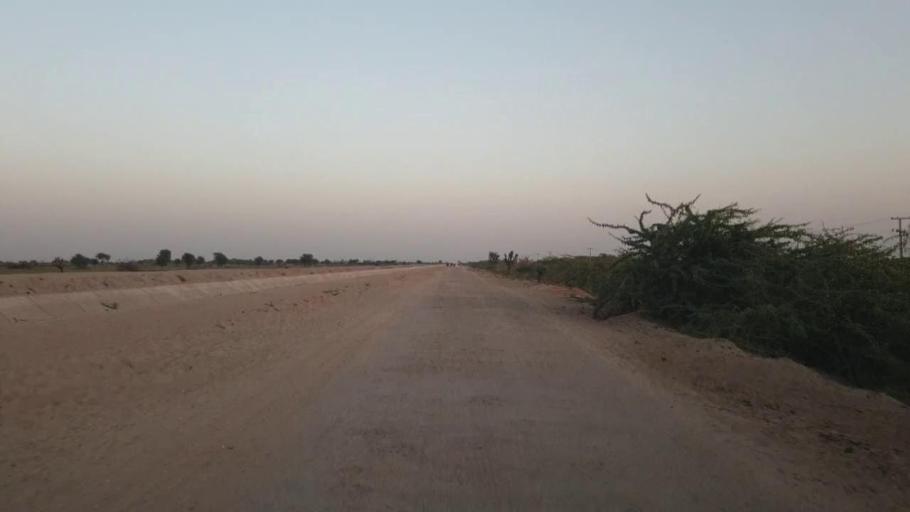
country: PK
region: Sindh
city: Dhoro Naro
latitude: 25.4457
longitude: 69.6294
